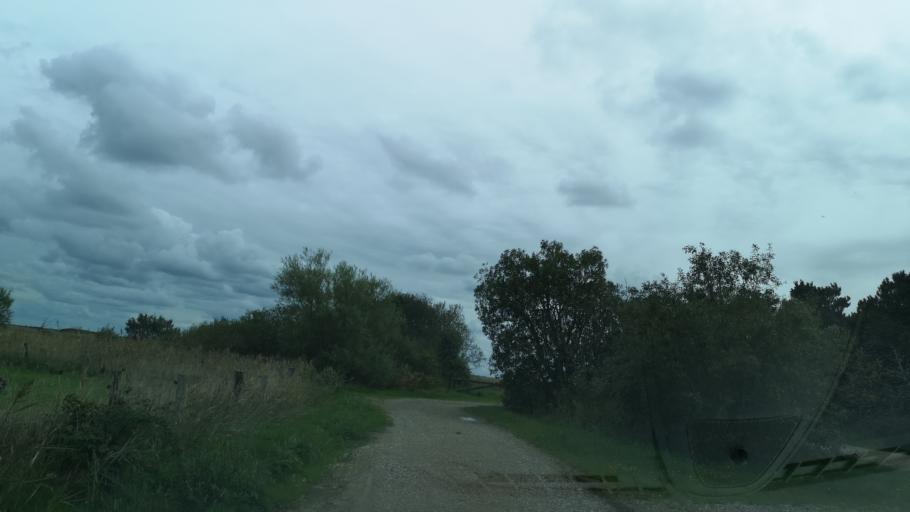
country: DK
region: Central Jutland
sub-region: Ringkobing-Skjern Kommune
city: Hvide Sande
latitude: 55.8598
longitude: 8.2393
